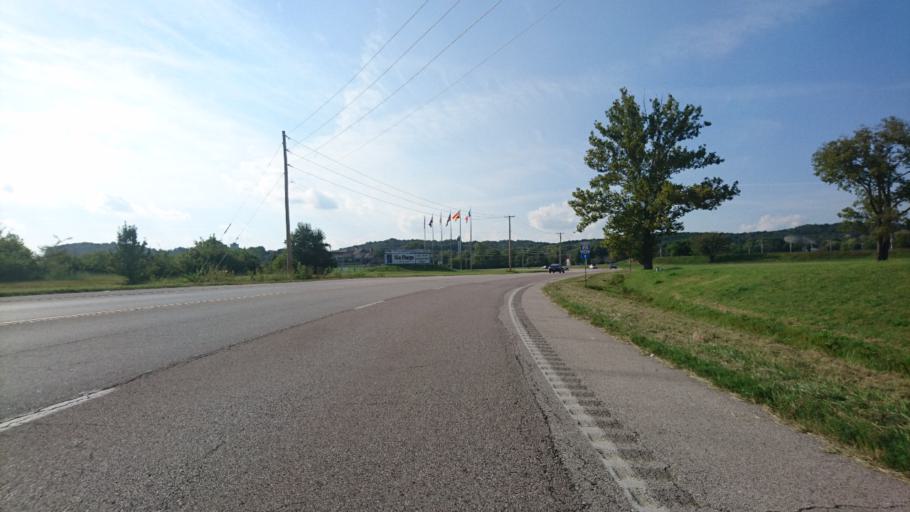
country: US
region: Missouri
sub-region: Saint Louis County
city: Eureka
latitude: 38.5061
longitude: -90.6738
